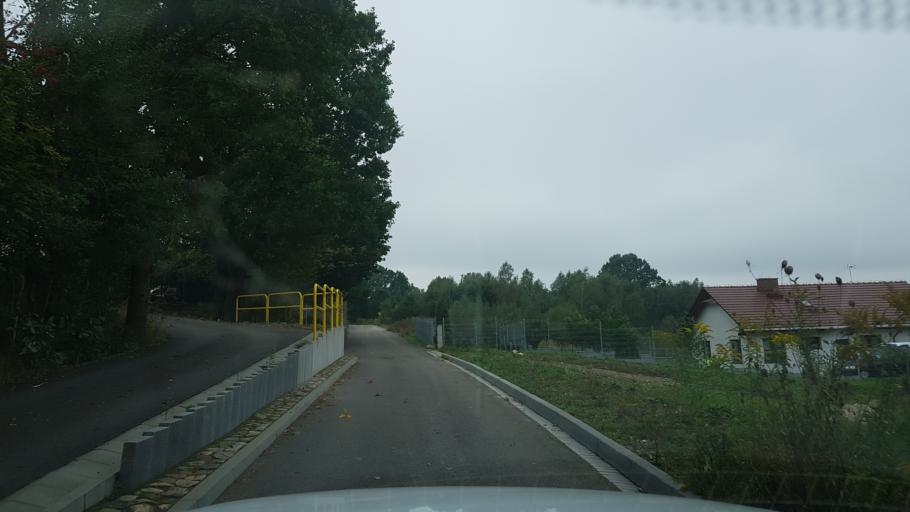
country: PL
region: West Pomeranian Voivodeship
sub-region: Powiat swidwinski
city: Polczyn-Zdroj
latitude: 53.7822
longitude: 16.0707
